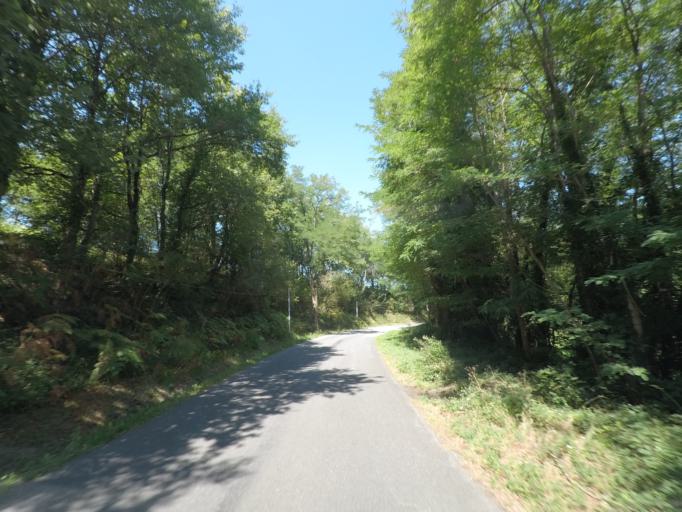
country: FR
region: Midi-Pyrenees
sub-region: Departement de l'Aveyron
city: Livinhac-le-Haut
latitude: 44.6118
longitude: 2.2214
